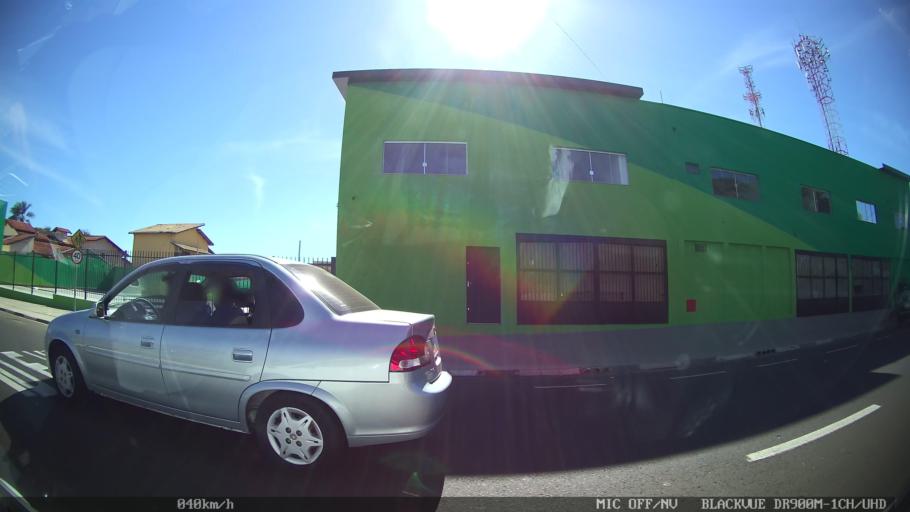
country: BR
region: Sao Paulo
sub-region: Franca
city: Franca
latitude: -20.5613
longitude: -47.3708
